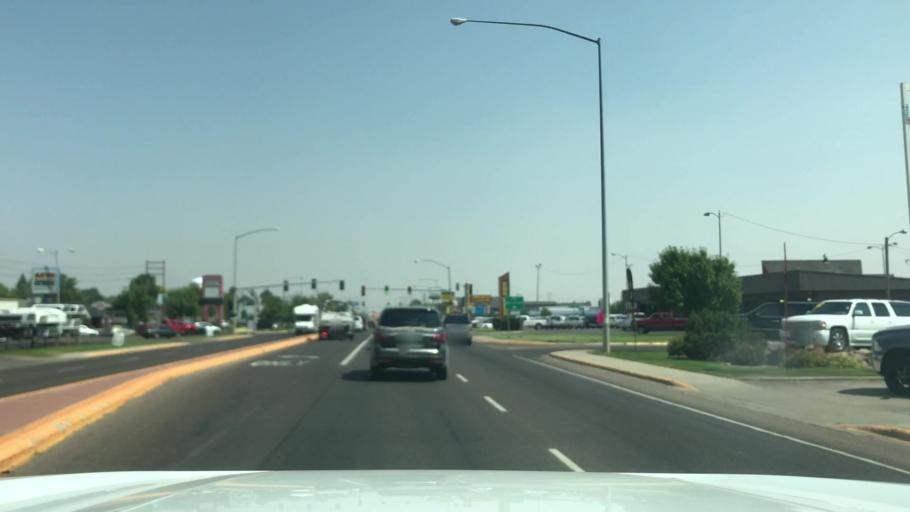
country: US
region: Montana
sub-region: Cascade County
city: Great Falls
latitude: 47.4940
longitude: -111.2434
